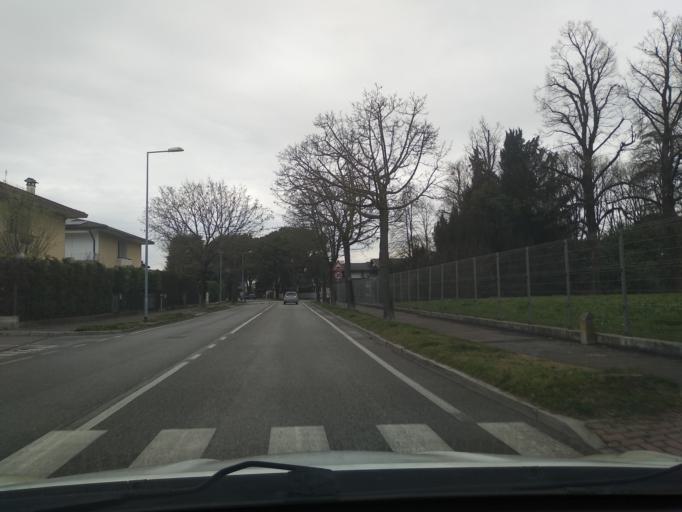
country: IT
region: Veneto
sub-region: Provincia di Padova
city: Selvazzano Dentro
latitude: 45.3906
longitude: 11.7839
